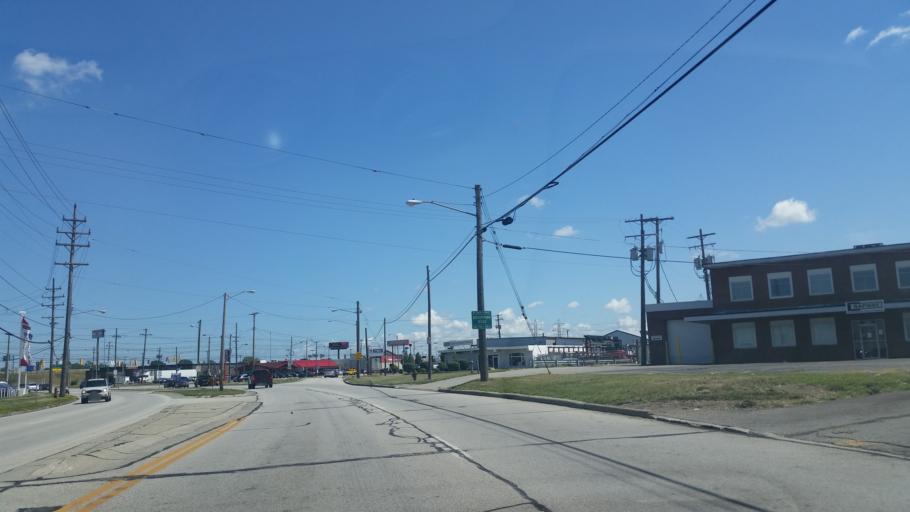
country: US
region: Ohio
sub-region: Cuyahoga County
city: Brook Park
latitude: 41.4172
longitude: -81.7822
